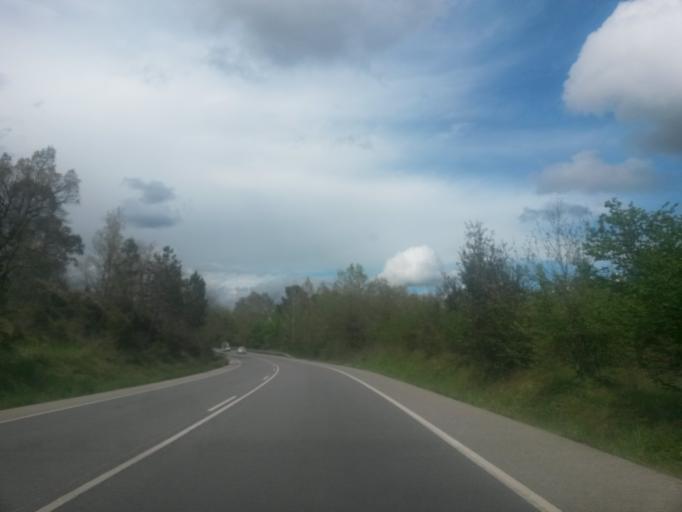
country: ES
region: Catalonia
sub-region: Provincia de Girona
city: Brunyola
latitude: 41.9039
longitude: 2.6623
